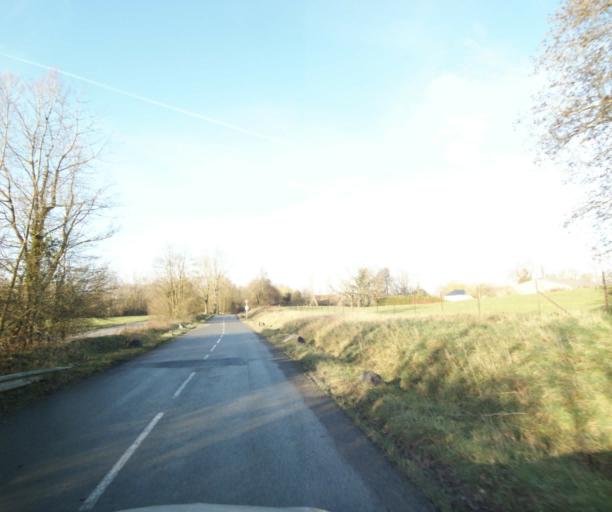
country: FR
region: Nord-Pas-de-Calais
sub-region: Departement du Nord
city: Curgies
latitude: 50.3280
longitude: 3.5949
